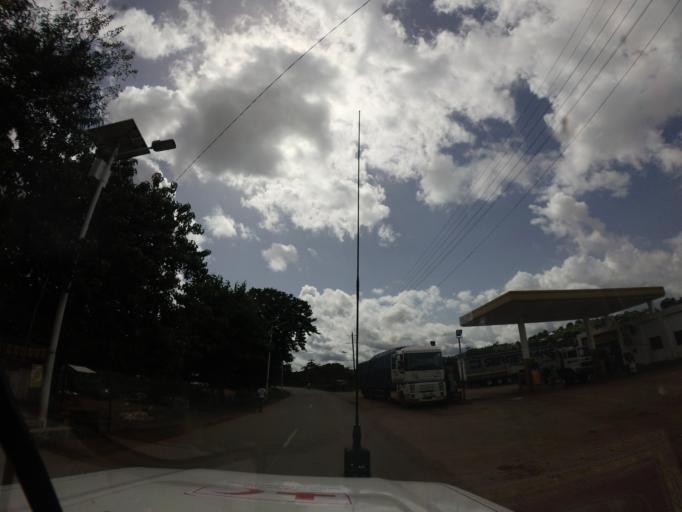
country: GN
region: Mamou
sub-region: Mamou Prefecture
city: Mamou
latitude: 10.3710
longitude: -12.0696
